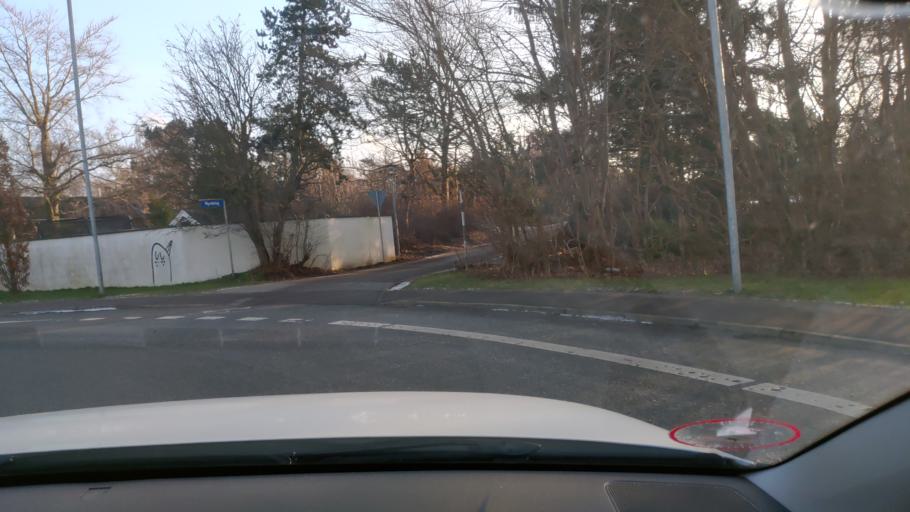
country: DK
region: Zealand
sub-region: Solrod Kommune
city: Solrod Strand
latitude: 55.5464
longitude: 12.2379
